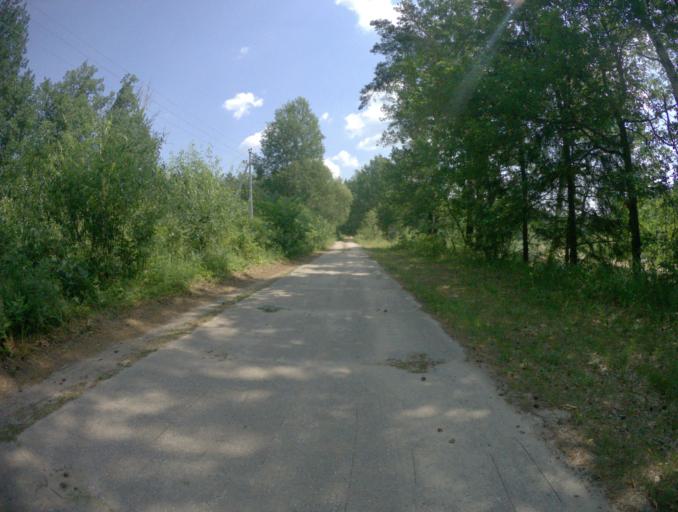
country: RU
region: Nizjnij Novgorod
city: Frolishchi
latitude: 56.4029
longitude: 42.5807
